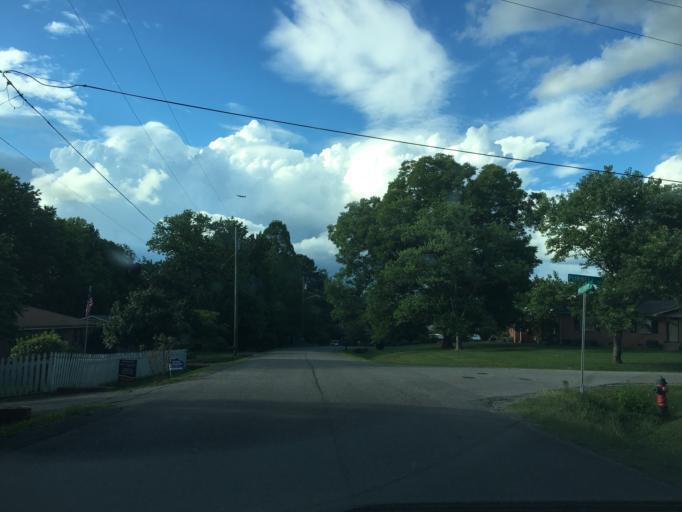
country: US
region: Tennessee
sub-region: Davidson County
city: Oak Hill
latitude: 36.0641
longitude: -86.7214
